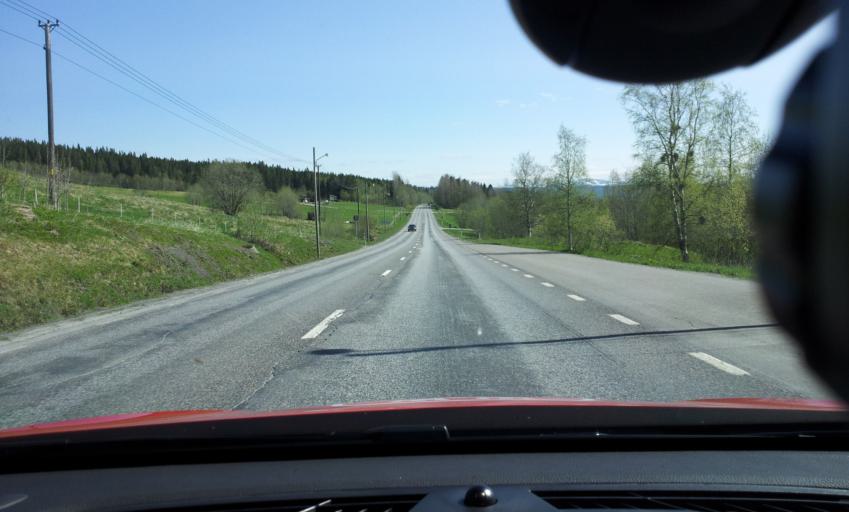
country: SE
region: Jaemtland
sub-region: Are Kommun
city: Are
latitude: 63.3646
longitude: 13.1718
